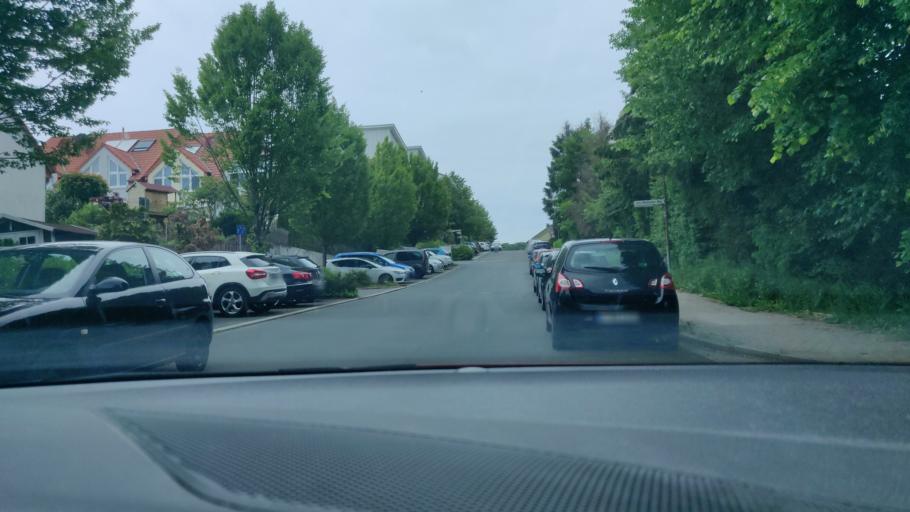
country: DE
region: North Rhine-Westphalia
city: Wulfrath
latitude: 51.2984
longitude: 7.0966
